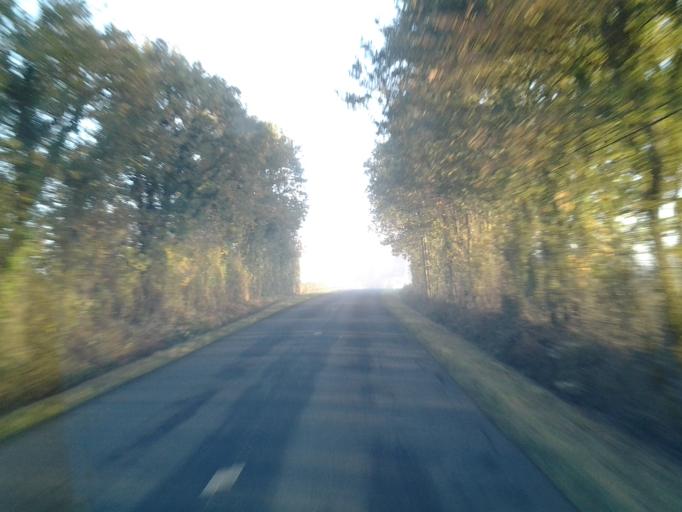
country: FR
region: Pays de la Loire
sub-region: Departement de la Vendee
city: Bournezeau
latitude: 46.6462
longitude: -1.2310
